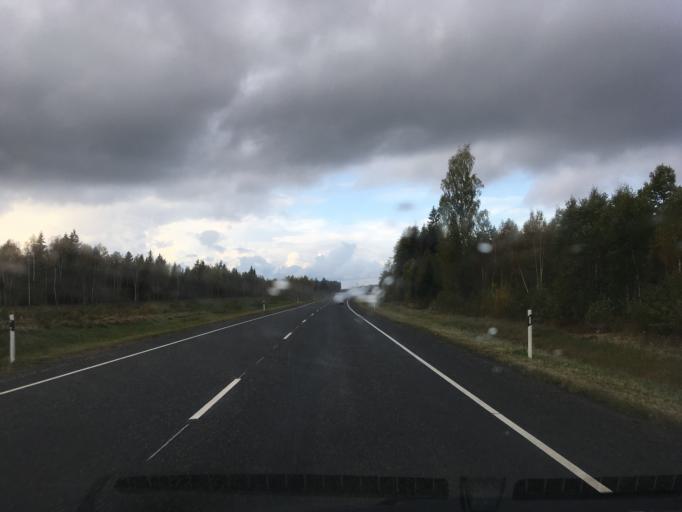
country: EE
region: Harju
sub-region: Nissi vald
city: Turba
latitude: 58.9419
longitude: 24.0878
